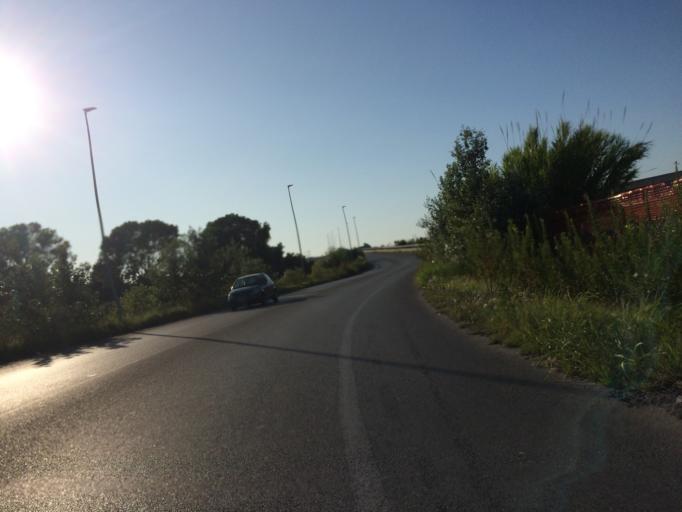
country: IT
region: Tuscany
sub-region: Provincia di Lucca
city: Viareggio
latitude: 43.8600
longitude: 10.2650
